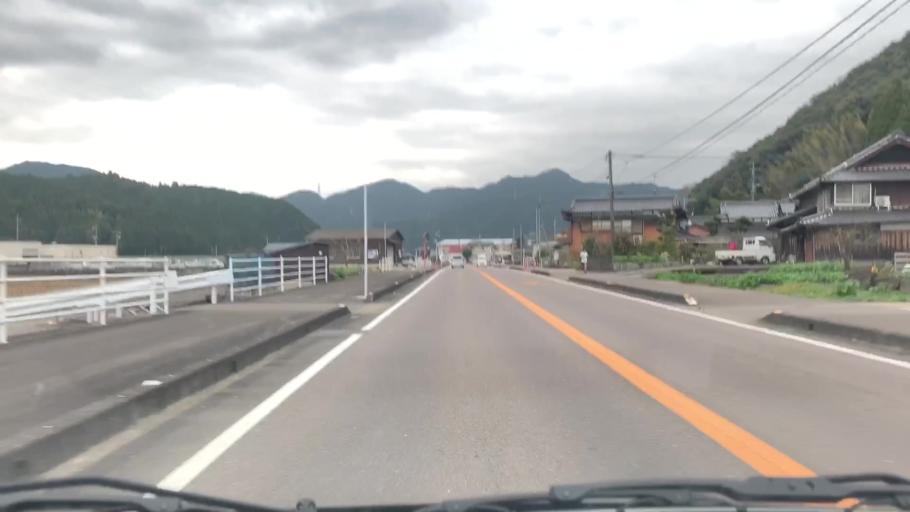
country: JP
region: Saga Prefecture
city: Kashima
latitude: 33.1275
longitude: 130.0492
